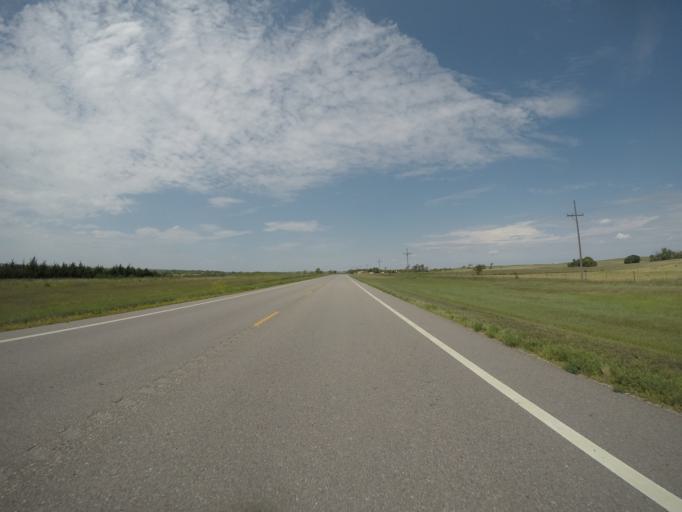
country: US
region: Kansas
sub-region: Rooks County
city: Stockton
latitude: 39.4440
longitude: -99.2159
